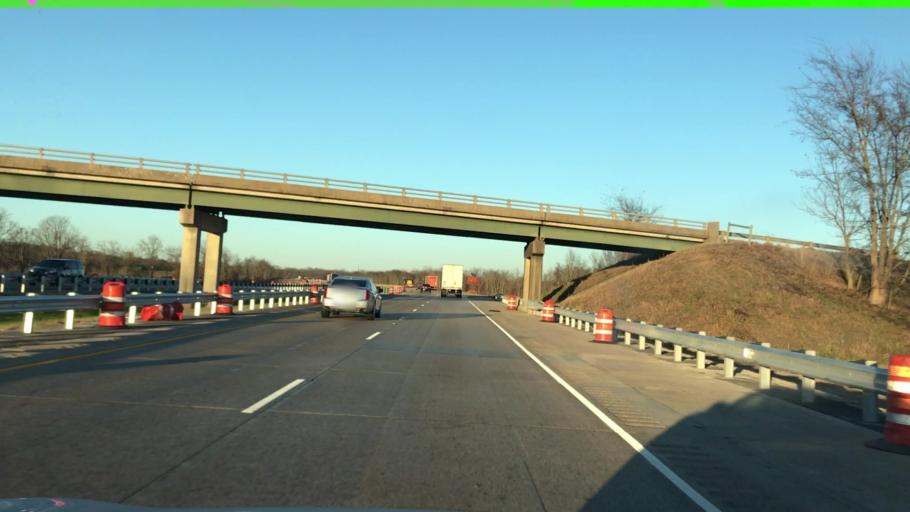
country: US
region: Arkansas
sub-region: Miller County
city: Texarkana
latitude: 33.5733
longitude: -93.8482
